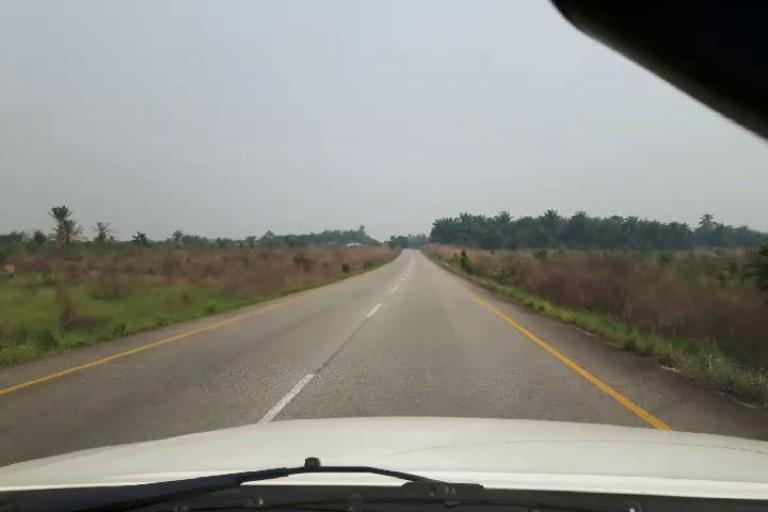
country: SL
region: Southern Province
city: Largo
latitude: 8.2238
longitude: -12.0755
